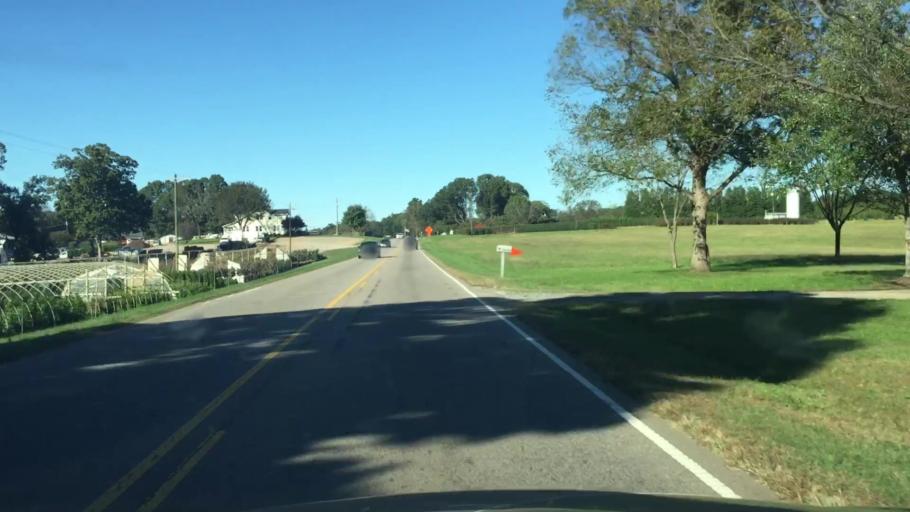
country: US
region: North Carolina
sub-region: Gaston County
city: Davidson
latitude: 35.5022
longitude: -80.7690
